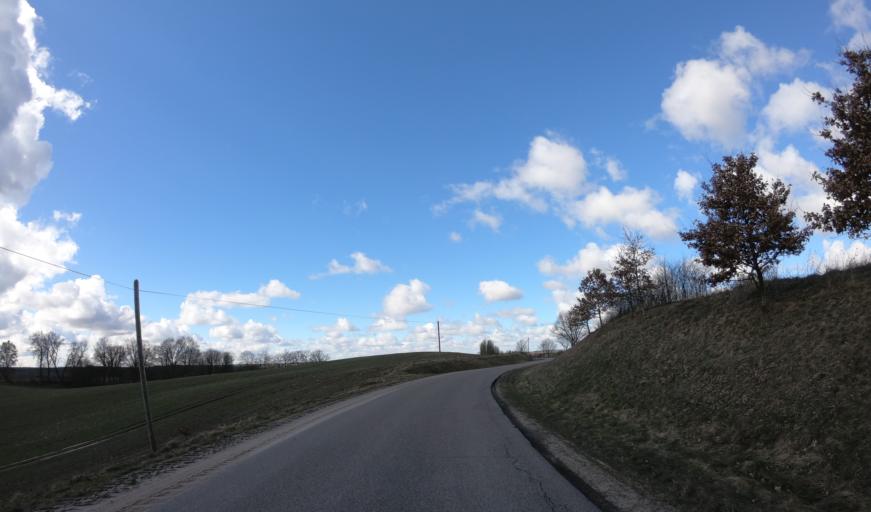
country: PL
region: West Pomeranian Voivodeship
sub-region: Powiat drawski
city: Drawsko Pomorskie
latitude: 53.4835
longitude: 15.8861
